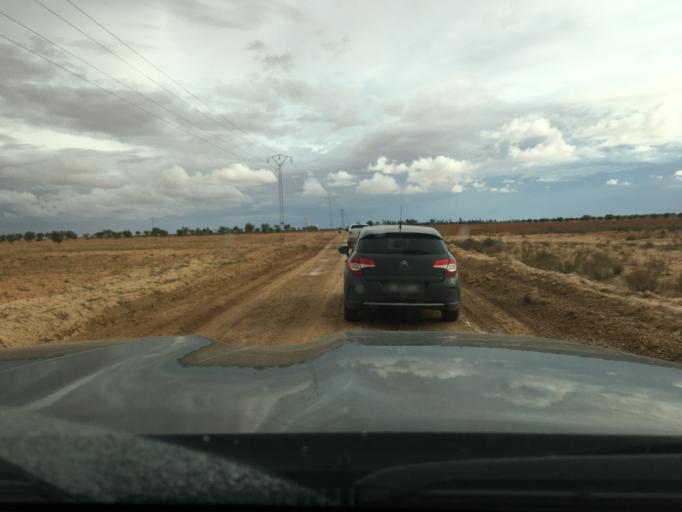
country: TN
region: Madanin
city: Medenine
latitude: 33.2793
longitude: 10.5568
